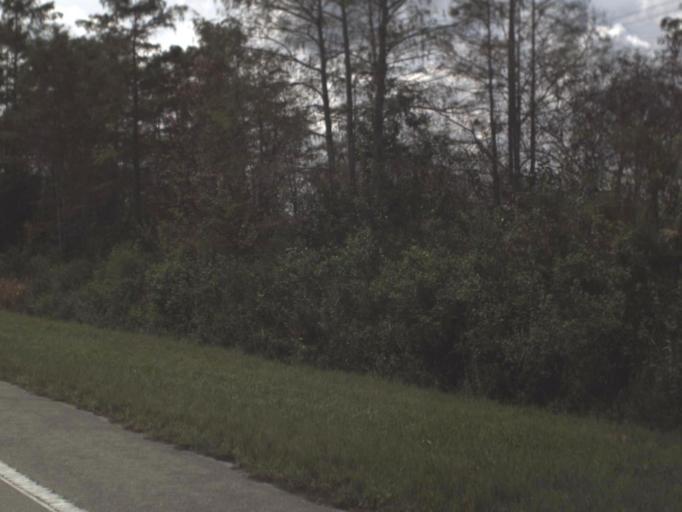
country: US
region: Florida
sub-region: Collier County
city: Orangetree
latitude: 26.0725
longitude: -81.3446
